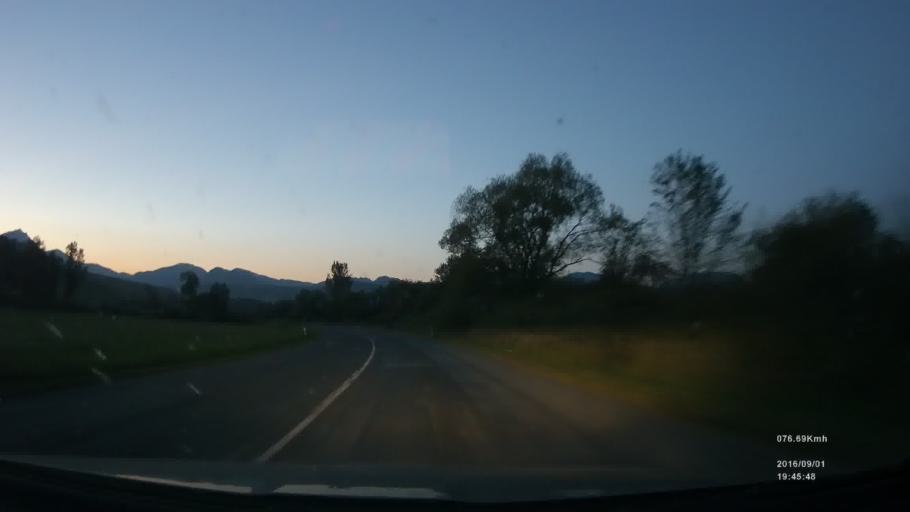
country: SK
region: Zilinsky
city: Ruzomberok
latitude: 49.0830
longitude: 19.4395
